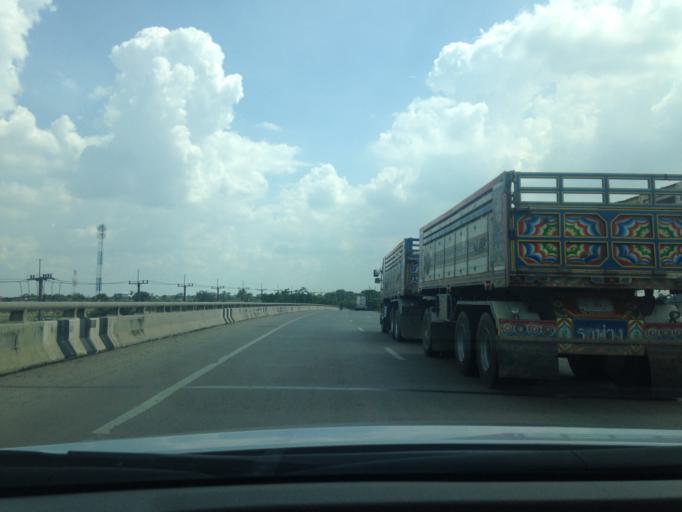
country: TH
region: Pathum Thani
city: Sam Khok
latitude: 14.0925
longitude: 100.5191
